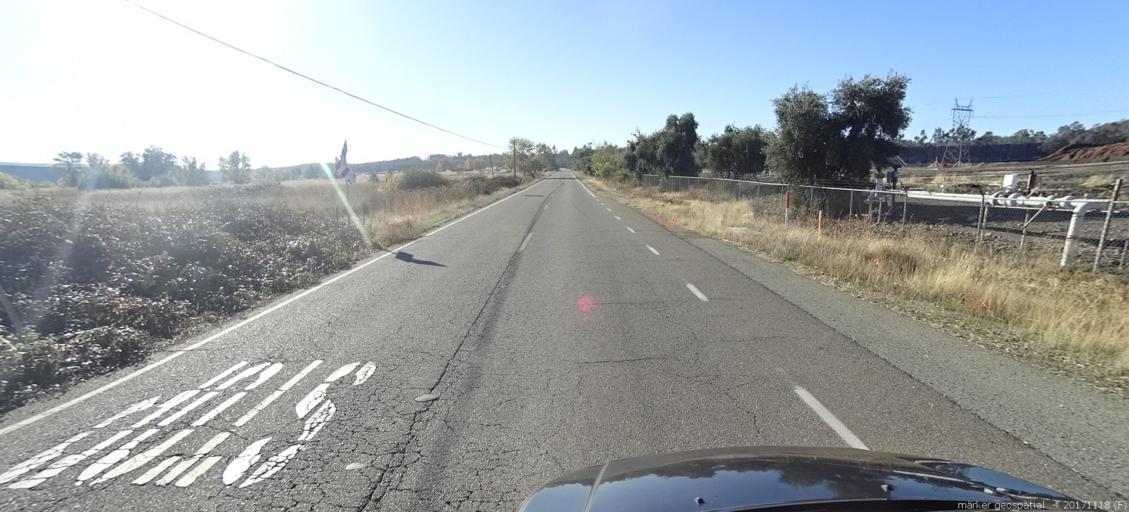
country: US
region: California
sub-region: Shasta County
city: Anderson
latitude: 40.4296
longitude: -122.2734
